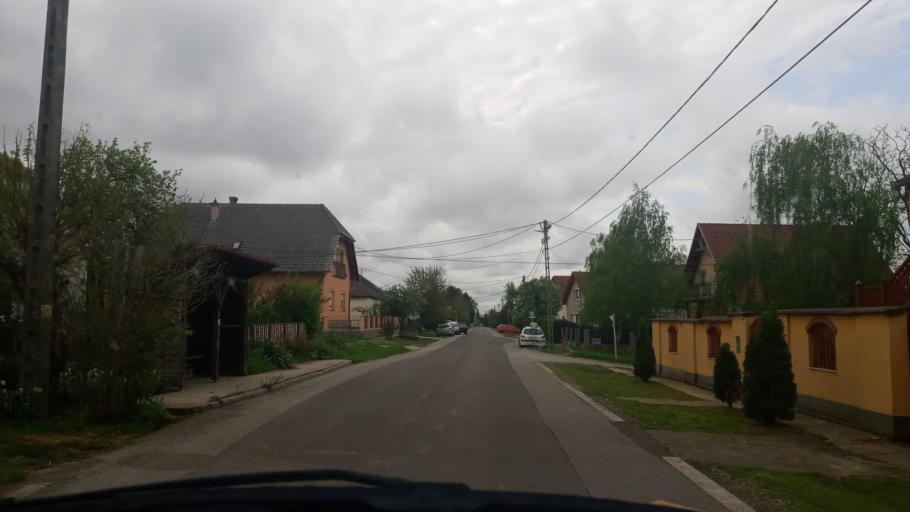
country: HU
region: Baranya
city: Kozarmisleny
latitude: 46.0029
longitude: 18.3749
